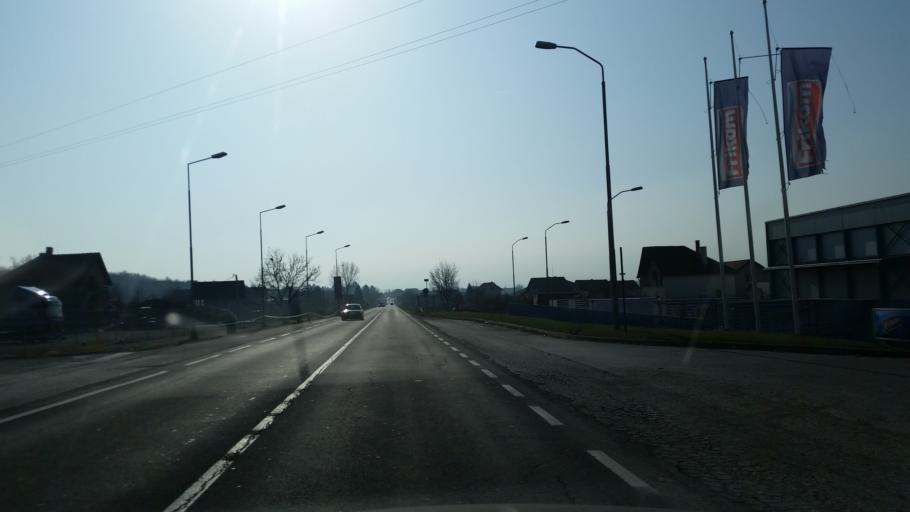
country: RS
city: Prislonica
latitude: 43.9252
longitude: 20.4095
